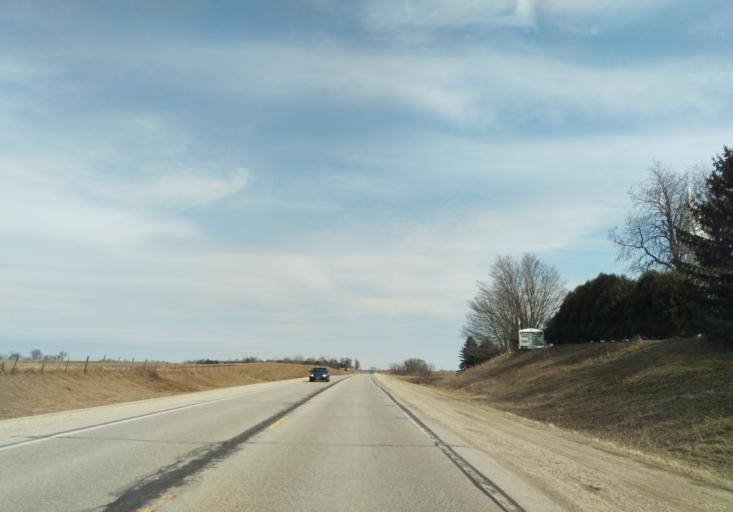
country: US
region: Iowa
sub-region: Allamakee County
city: Waukon
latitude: 43.2409
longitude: -91.5540
